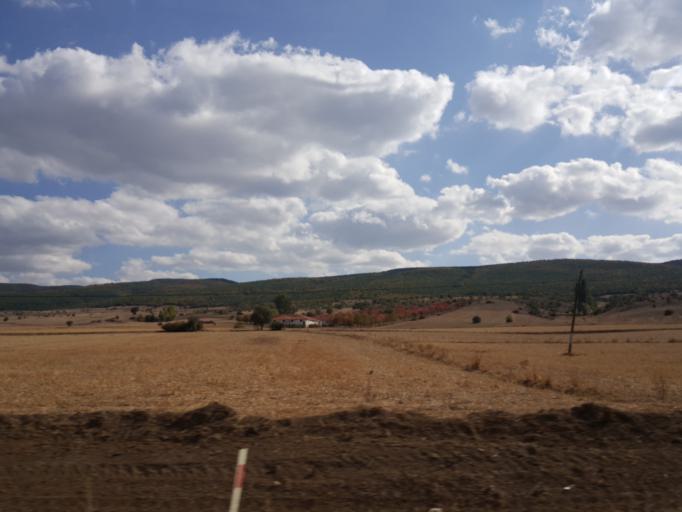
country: TR
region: Tokat
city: Yesilyurt
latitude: 40.0091
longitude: 36.1886
